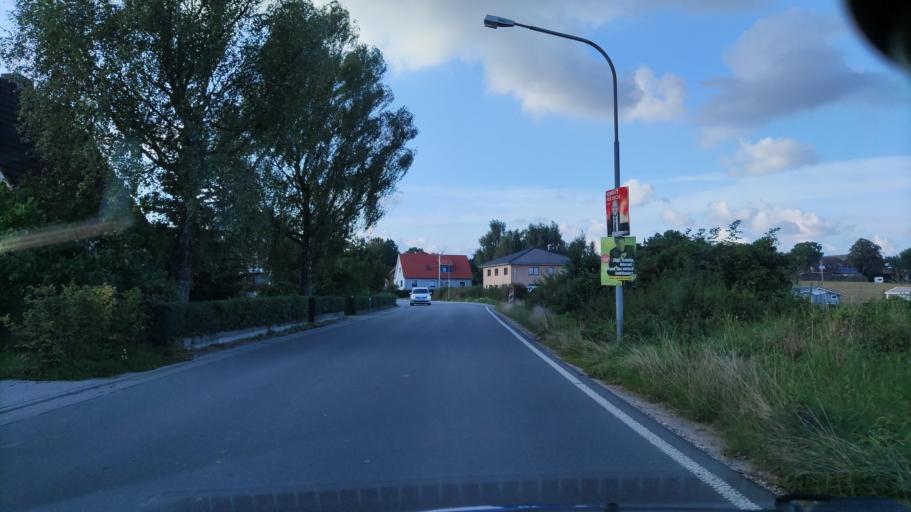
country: DE
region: Schleswig-Holstein
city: Glasau
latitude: 54.0723
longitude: 10.5012
